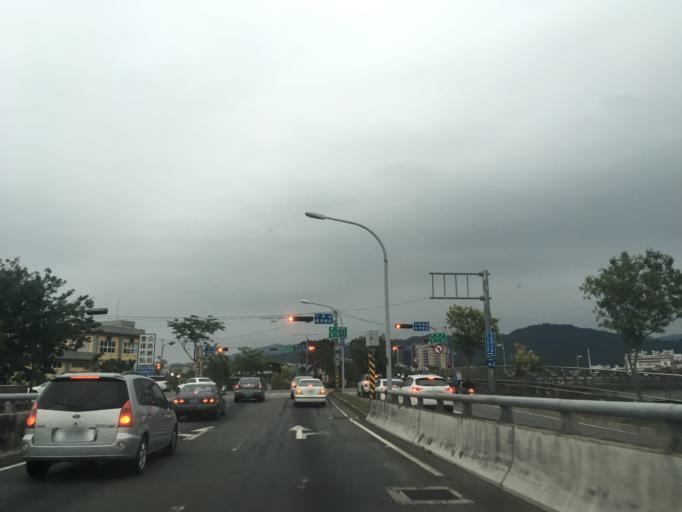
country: TW
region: Taiwan
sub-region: Taichung City
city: Taichung
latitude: 24.1346
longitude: 120.7094
